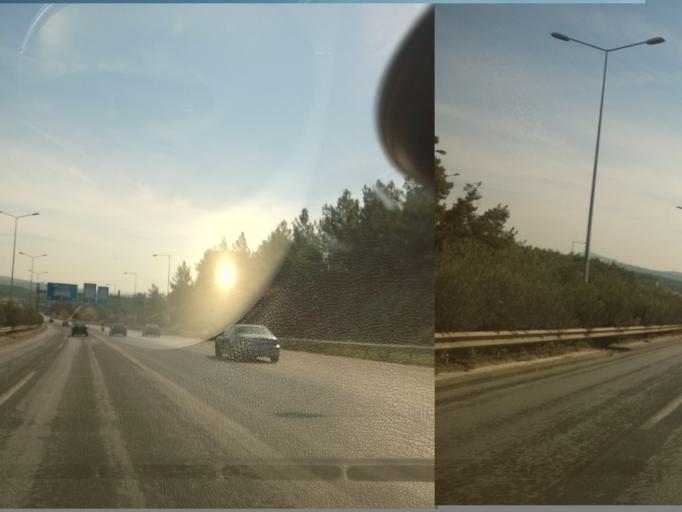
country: GR
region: Central Macedonia
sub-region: Nomos Thessalonikis
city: Triandria
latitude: 40.6307
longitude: 22.9747
